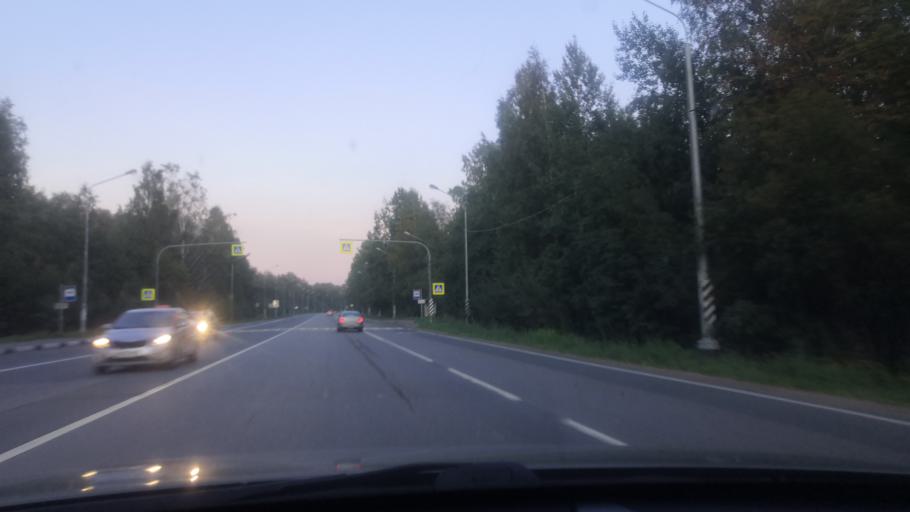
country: RU
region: St.-Petersburg
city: Beloostrov
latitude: 60.1959
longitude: 30.0571
